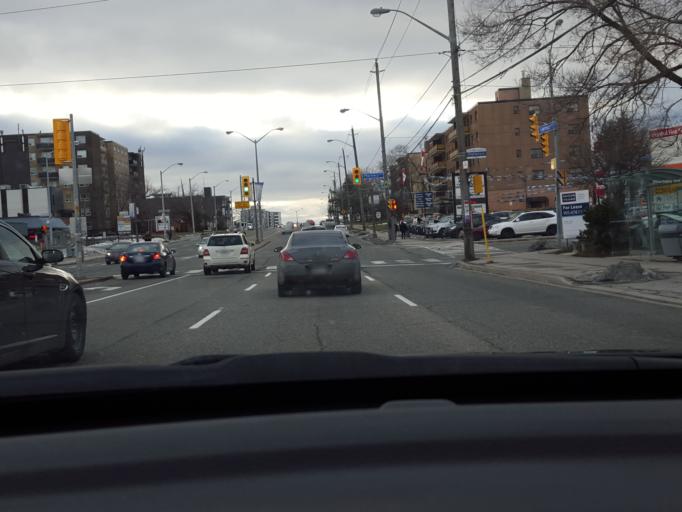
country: CA
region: Ontario
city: Scarborough
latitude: 43.7435
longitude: -79.3039
